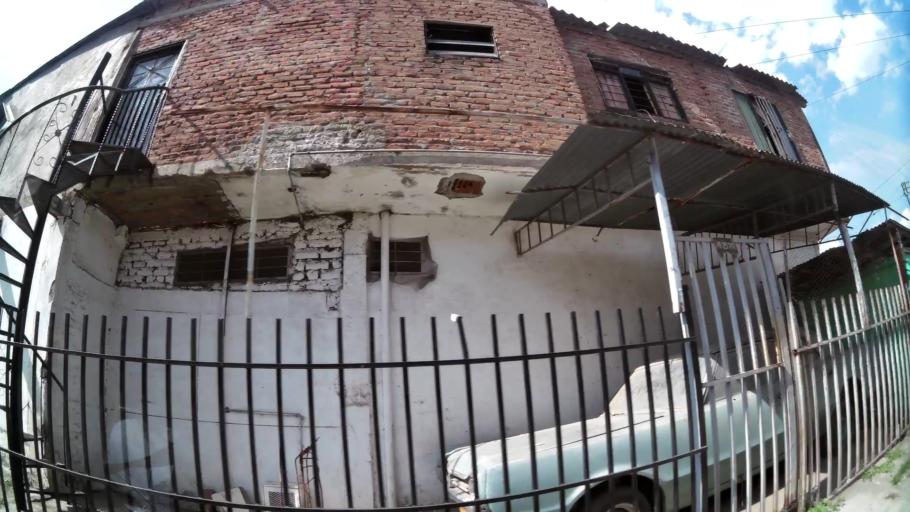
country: CO
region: Valle del Cauca
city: Cali
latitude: 3.4168
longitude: -76.5155
